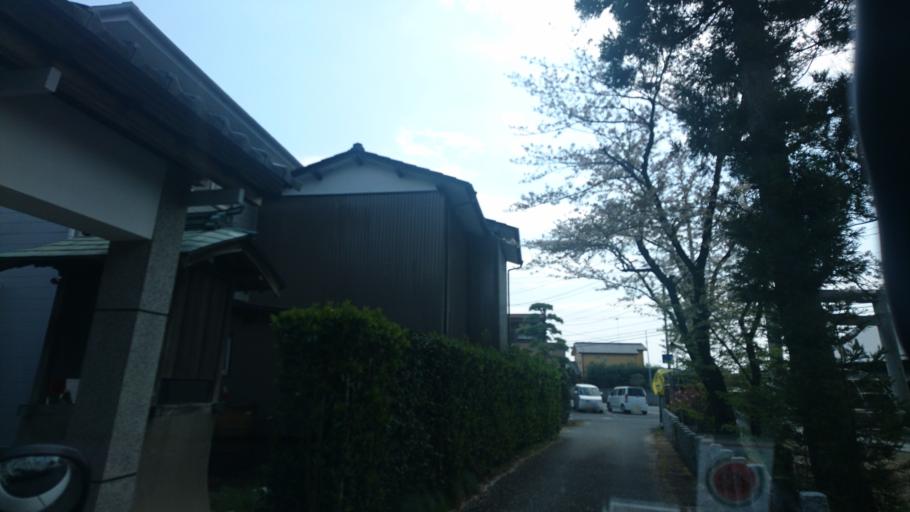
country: JP
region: Ibaraki
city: Yuki
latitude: 36.2866
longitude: 139.8965
